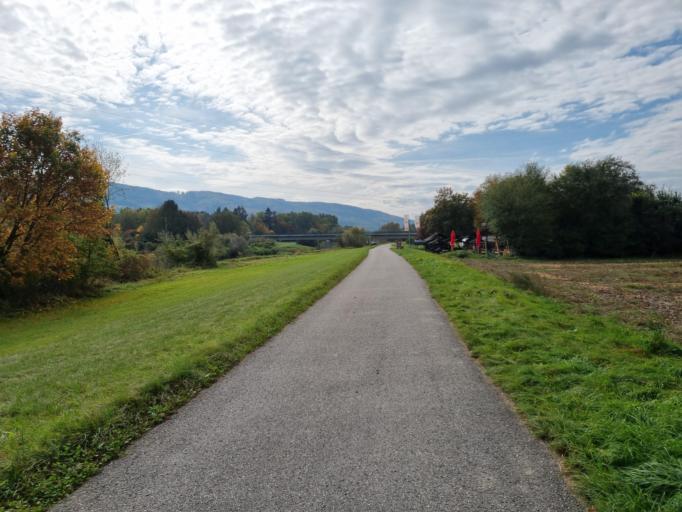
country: AT
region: Lower Austria
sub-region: Politischer Bezirk Sankt Polten
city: Wilhelmsburg
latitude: 48.1338
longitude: 15.6315
